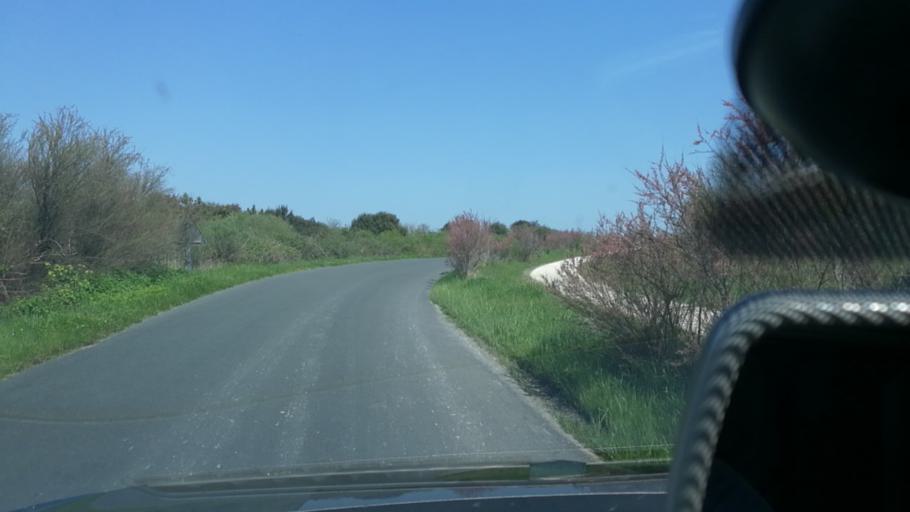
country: FR
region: Poitou-Charentes
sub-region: Departement de la Charente-Maritime
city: Saint-Trojan-les-Bains
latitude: 45.8643
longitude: -1.2272
